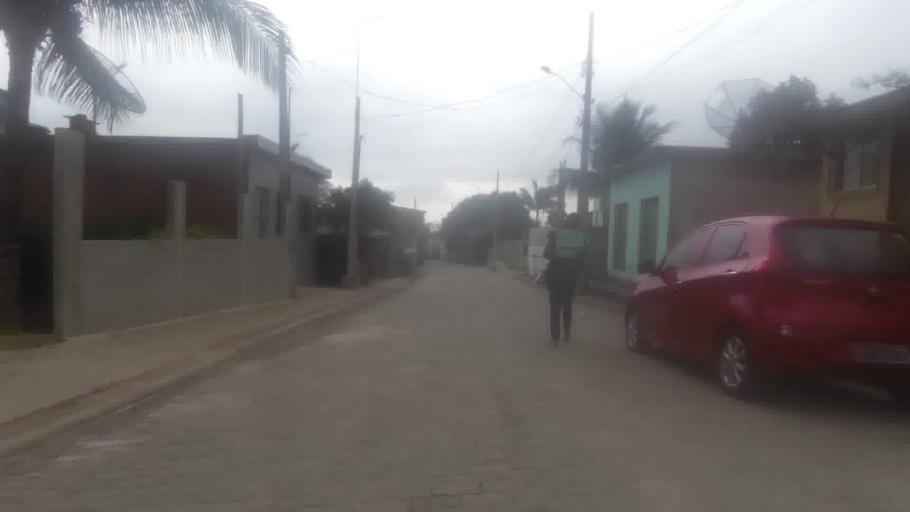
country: BR
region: Espirito Santo
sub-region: Piuma
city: Piuma
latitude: -20.7953
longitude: -40.6025
